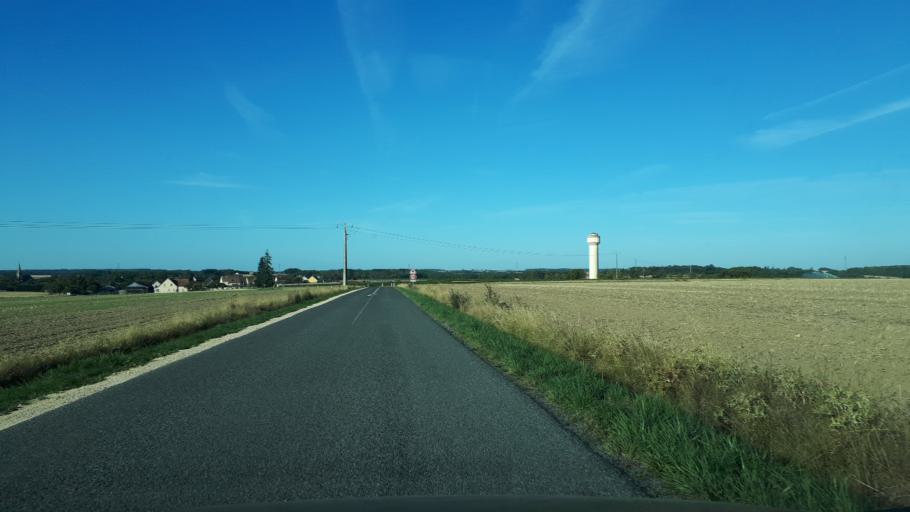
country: FR
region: Centre
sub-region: Departement du Loir-et-Cher
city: Lunay
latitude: 47.7595
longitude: 0.9426
